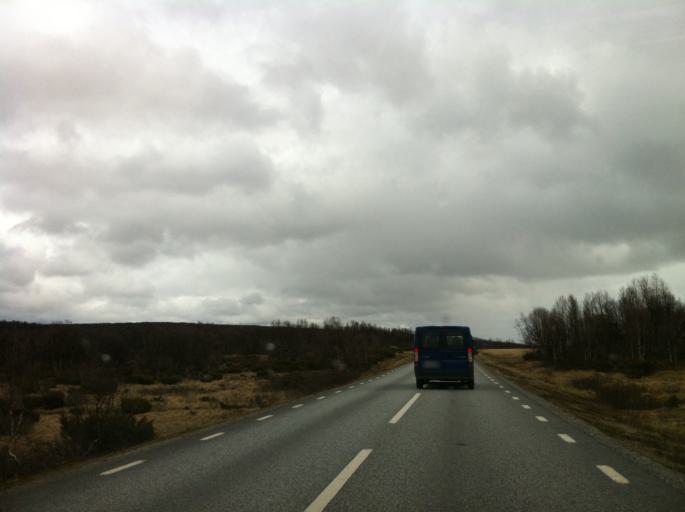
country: NO
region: Sor-Trondelag
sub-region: Tydal
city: Aas
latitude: 62.6381
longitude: 12.1025
